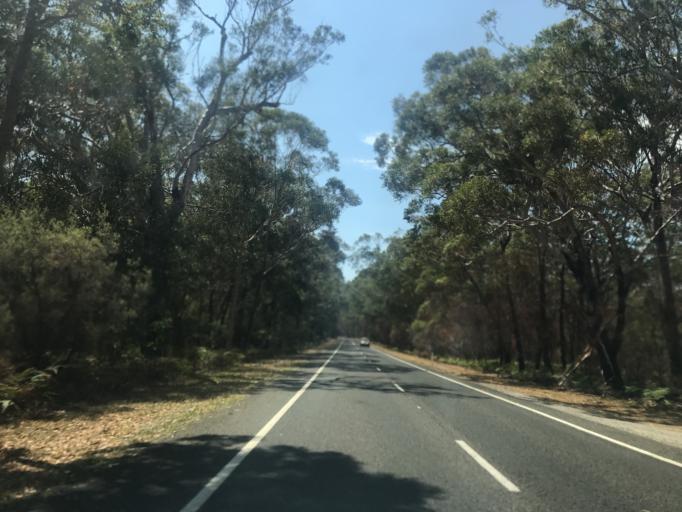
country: AU
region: Queensland
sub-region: Redland
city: Victoria Point
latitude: -27.4355
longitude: 153.5002
